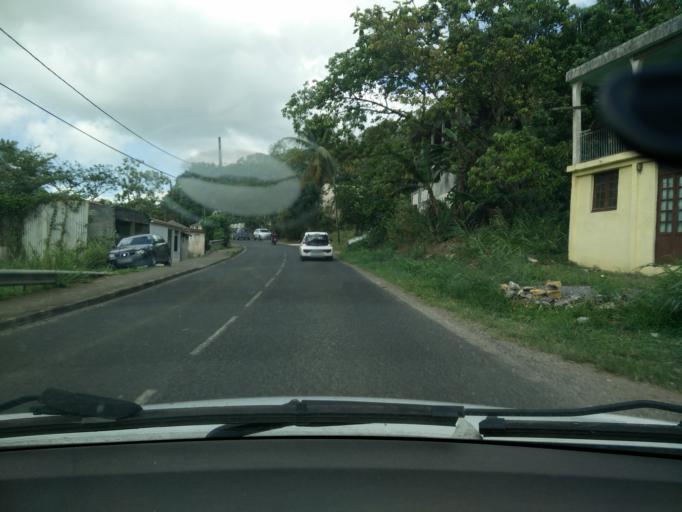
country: GP
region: Guadeloupe
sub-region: Guadeloupe
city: Les Abymes
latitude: 16.2630
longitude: -61.4958
